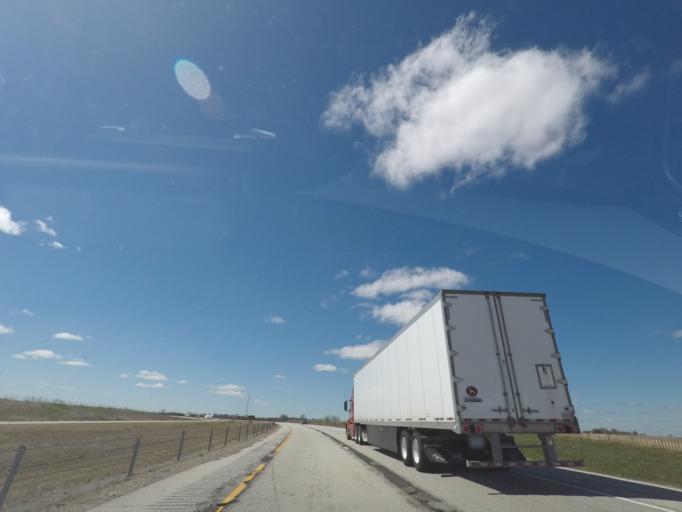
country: US
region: Illinois
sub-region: Livingston County
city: Odell
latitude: 41.0181
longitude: -88.5305
